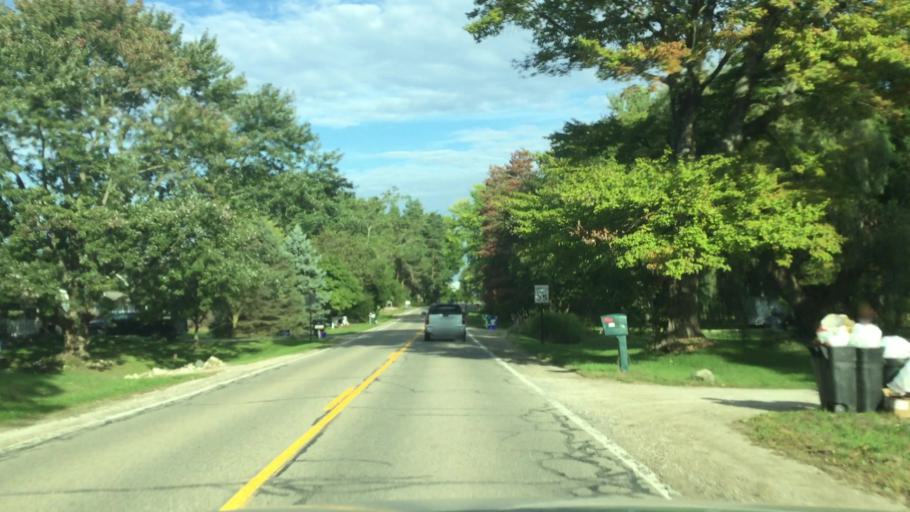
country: US
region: Michigan
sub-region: Livingston County
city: Howell
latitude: 42.5945
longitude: -83.9043
